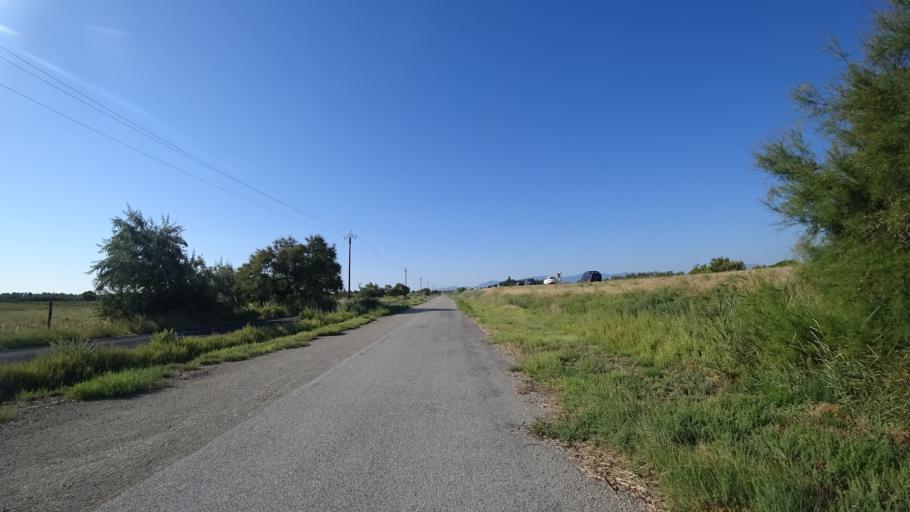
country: FR
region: Languedoc-Roussillon
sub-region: Departement des Pyrenees-Orientales
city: Sainte-Marie-Plage
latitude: 42.7448
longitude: 3.0233
